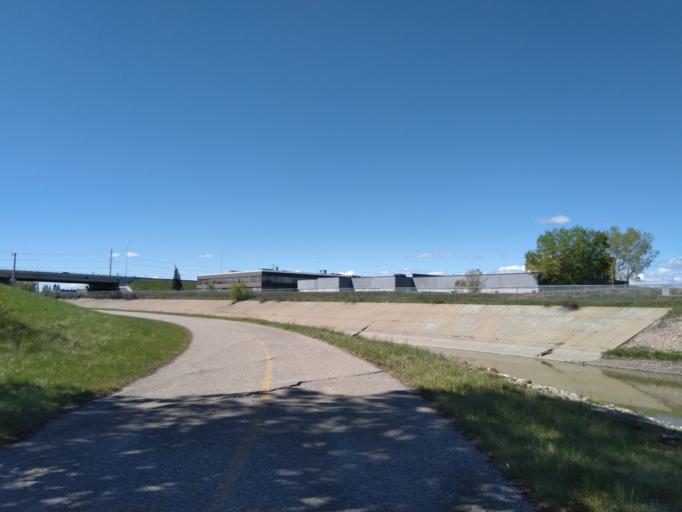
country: CA
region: Alberta
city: Calgary
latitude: 50.9818
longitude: -113.9933
